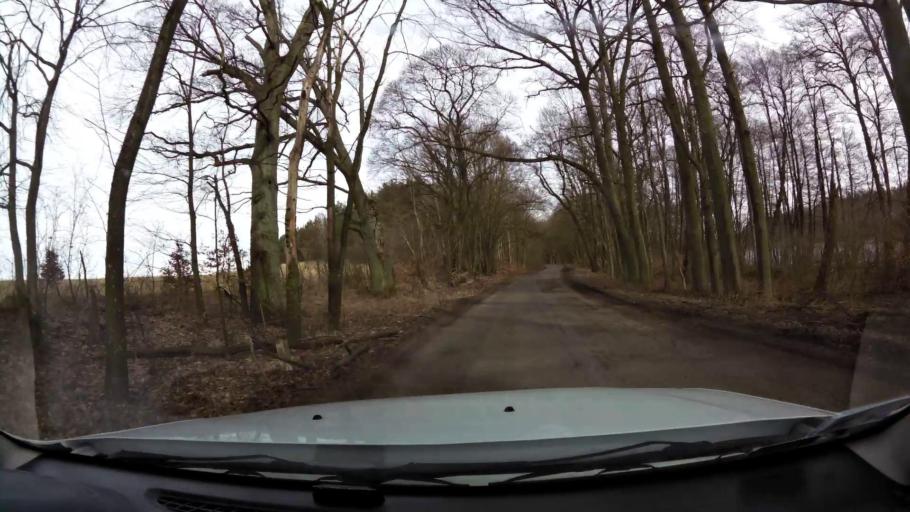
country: PL
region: West Pomeranian Voivodeship
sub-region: Powiat stargardzki
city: Insko
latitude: 53.4505
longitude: 15.6497
